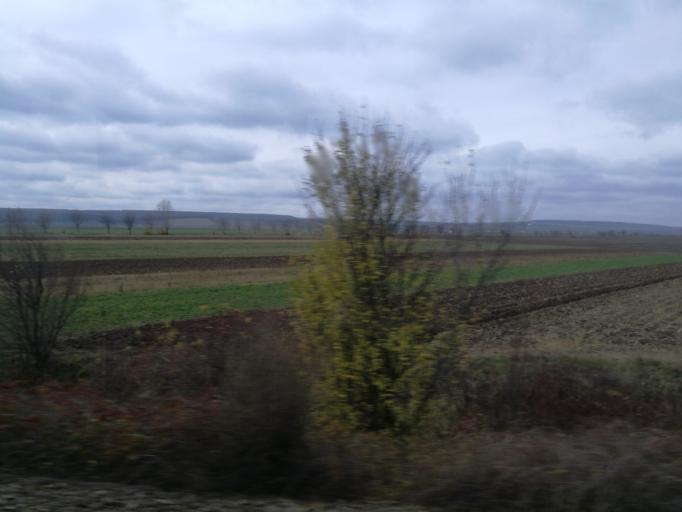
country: RO
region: Iasi
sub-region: Comuna Stolniceni-Prajescu
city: Stolniceni-Prajescu
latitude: 47.1833
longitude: 26.7486
